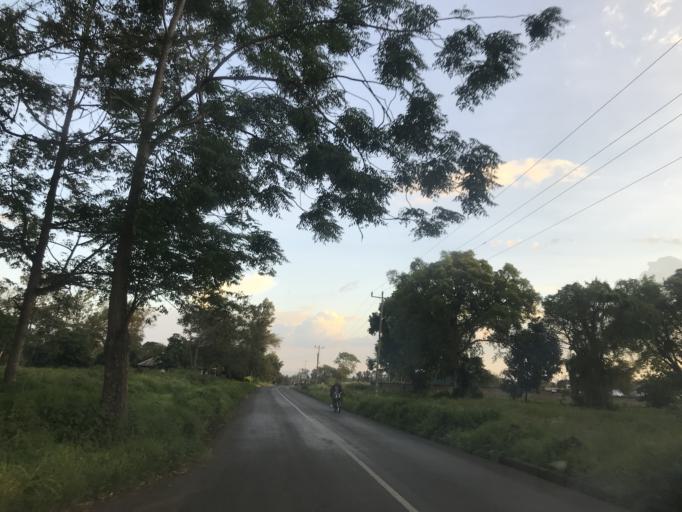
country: TZ
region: Arusha
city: Usa River
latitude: -3.3605
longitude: 36.8672
